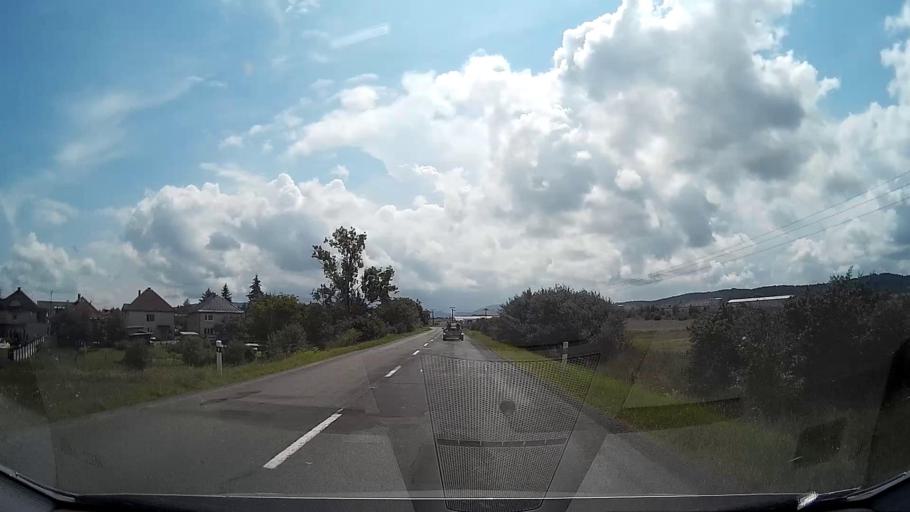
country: SK
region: Banskobystricky
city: Fil'akovo
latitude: 48.2679
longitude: 19.8118
